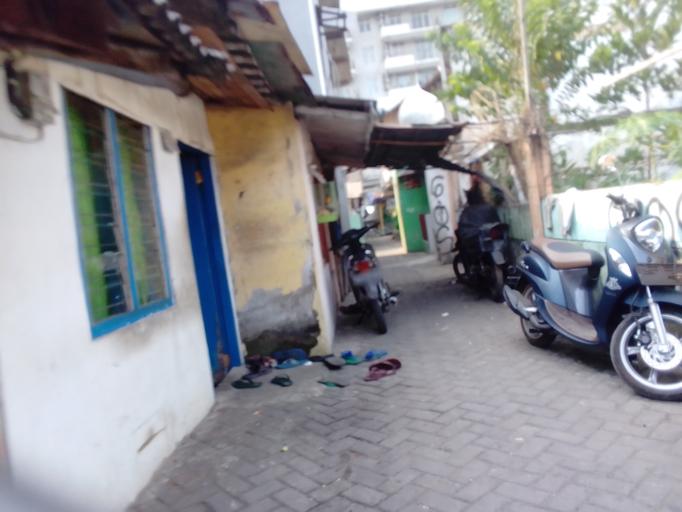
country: ID
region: Jakarta Raya
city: Jakarta
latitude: -6.1986
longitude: 106.8169
